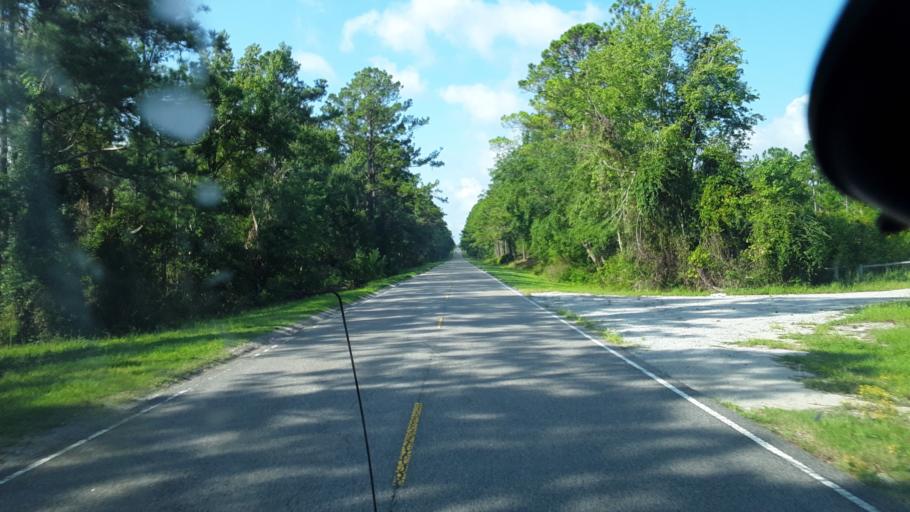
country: US
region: North Carolina
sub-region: Brunswick County
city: Boiling Spring Lakes
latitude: 34.0427
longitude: -78.0045
